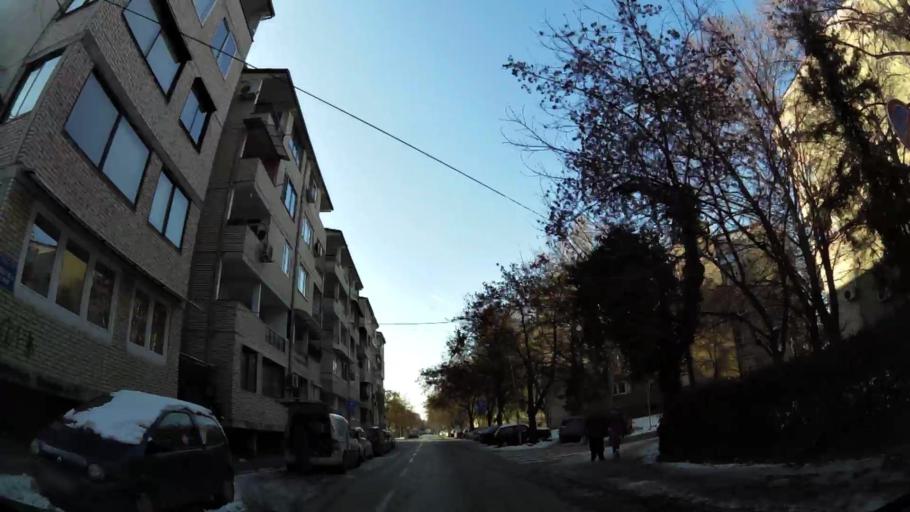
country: MK
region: Karpos
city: Skopje
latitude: 42.0071
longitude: 21.3899
